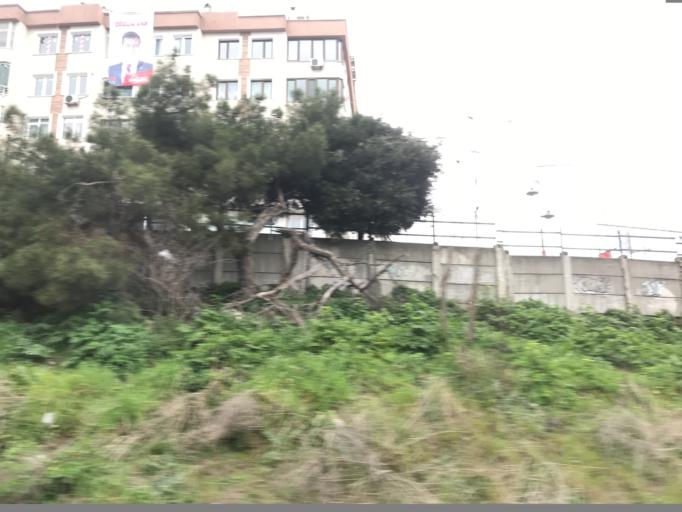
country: TR
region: Istanbul
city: Zeytinburnu
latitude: 40.9926
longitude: 28.9123
